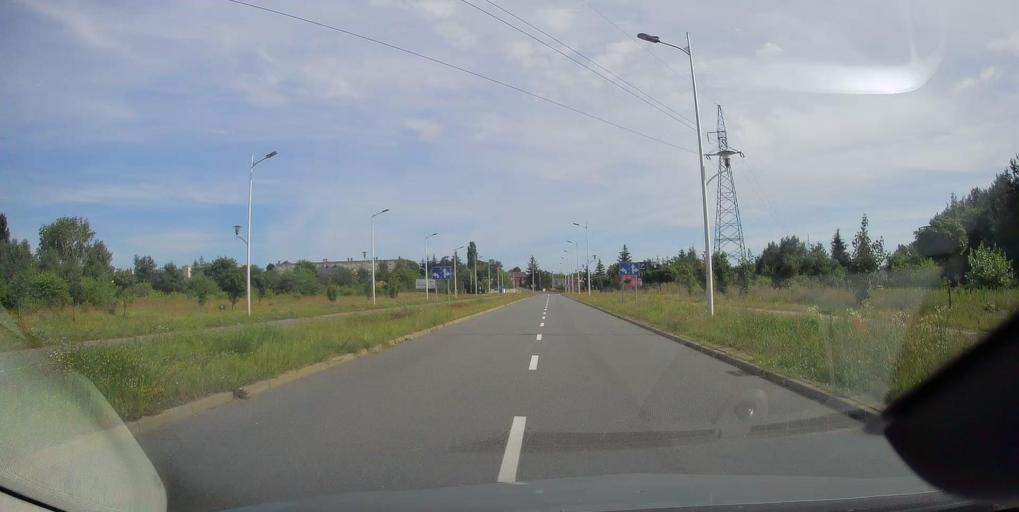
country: PL
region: Lodz Voivodeship
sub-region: Powiat tomaszowski
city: Tomaszow Mazowiecki
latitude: 51.5459
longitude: 19.9926
